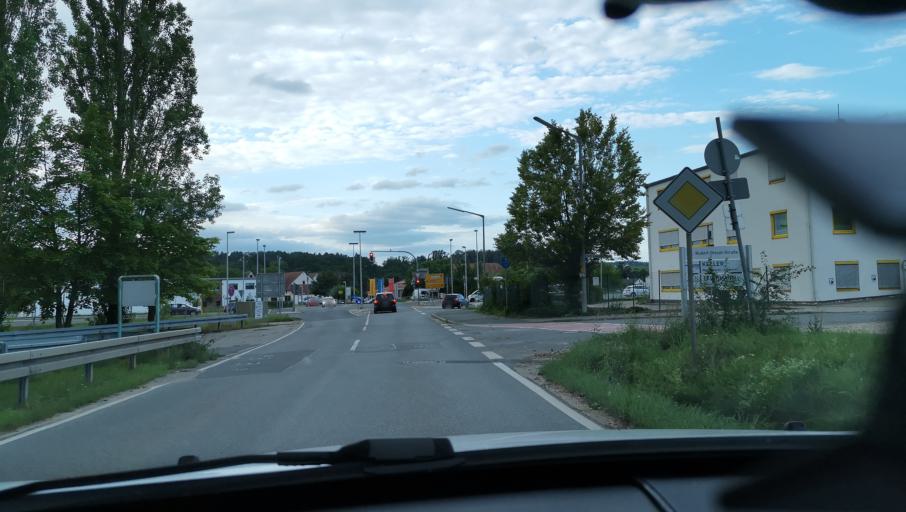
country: DE
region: Bavaria
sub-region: Regierungsbezirk Mittelfranken
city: Zirndorf
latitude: 49.4312
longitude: 10.9349
